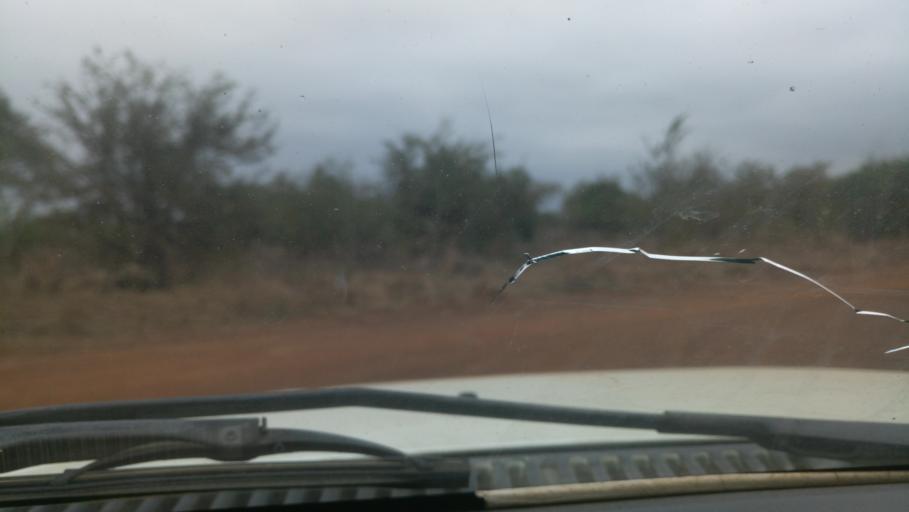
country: KE
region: Nairobi Area
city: Nairobi
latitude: -1.3846
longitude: 36.7874
